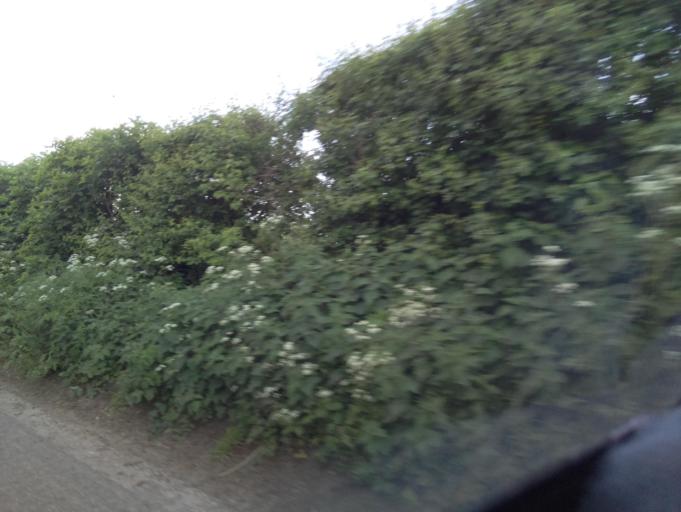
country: GB
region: England
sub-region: Wiltshire
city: Luckington
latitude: 51.5929
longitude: -2.2337
